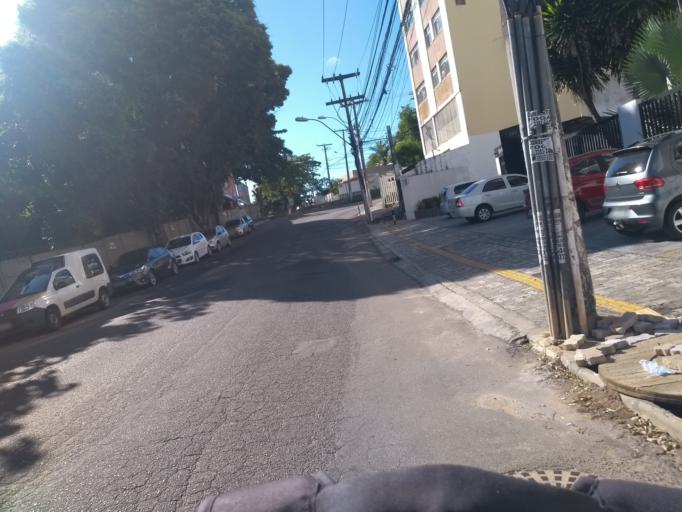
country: BR
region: Bahia
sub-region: Salvador
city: Salvador
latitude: -12.9970
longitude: -38.4601
